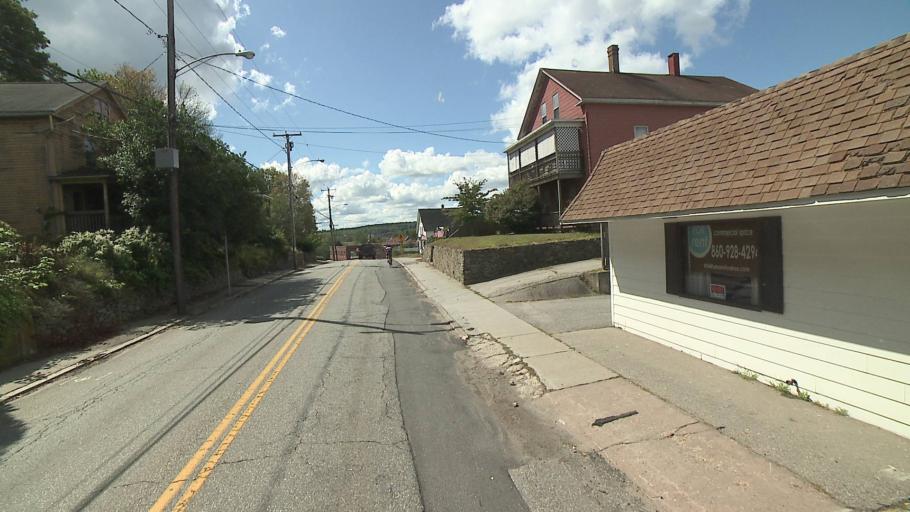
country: US
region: Connecticut
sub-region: Windham County
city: Putnam
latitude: 41.9173
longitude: -71.9055
